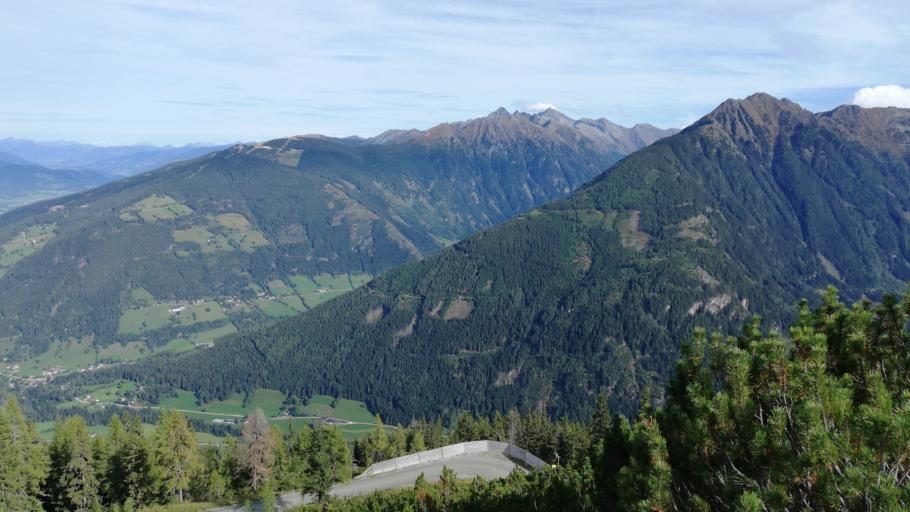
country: AT
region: Styria
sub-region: Politischer Bezirk Liezen
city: Schladming
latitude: 47.3580
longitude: 13.6404
